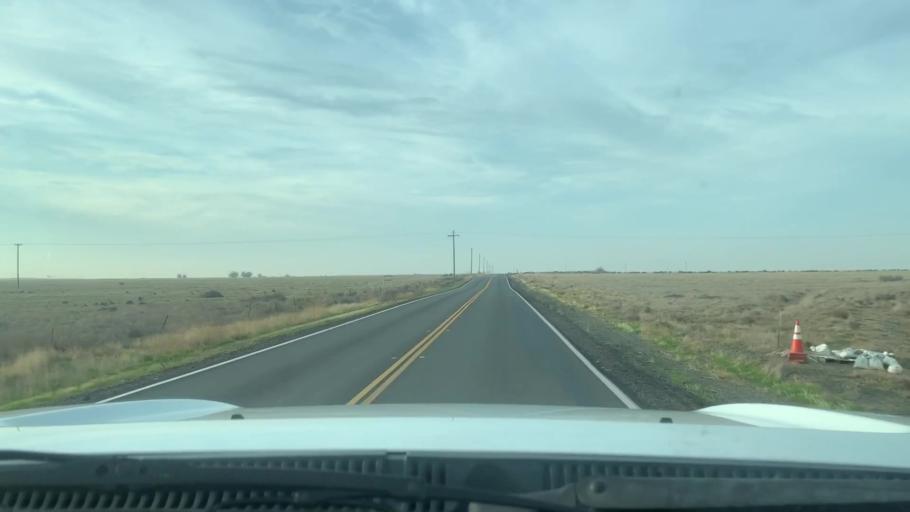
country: US
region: California
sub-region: Kern County
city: Lost Hills
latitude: 35.5581
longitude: -119.7977
